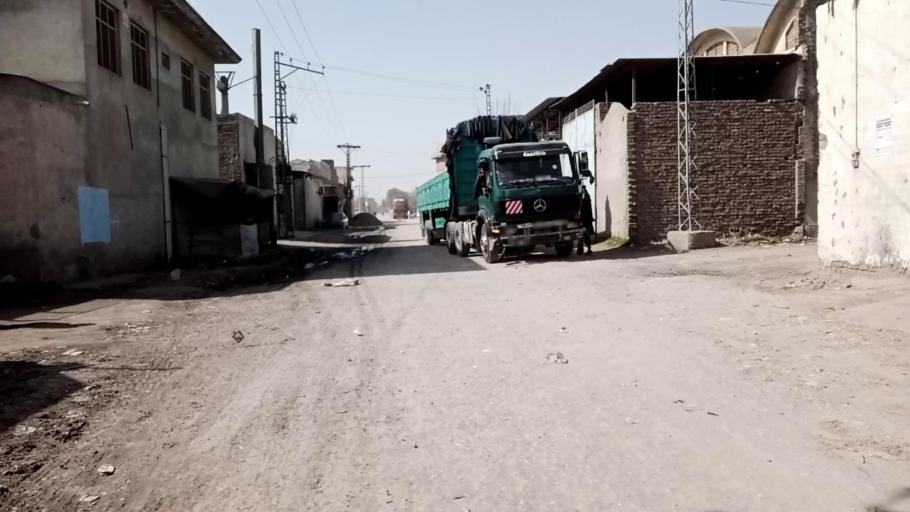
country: PK
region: Khyber Pakhtunkhwa
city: Peshawar
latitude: 34.0170
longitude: 71.6387
